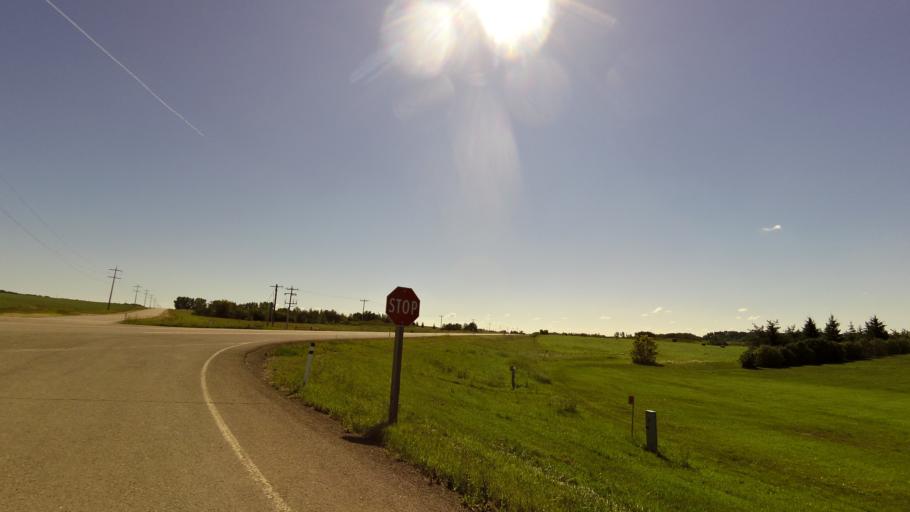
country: CA
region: Alberta
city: Wainwright
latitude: 52.8724
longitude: -110.9571
